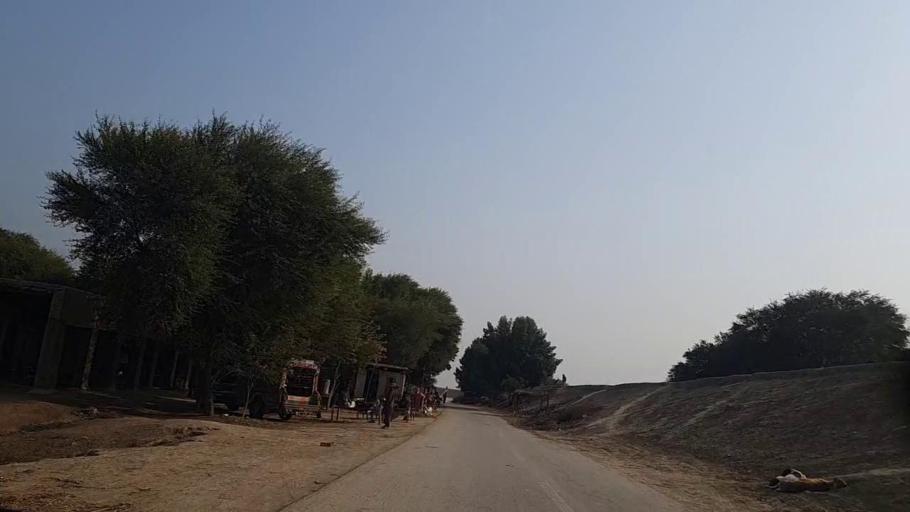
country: PK
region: Sindh
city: Sann
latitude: 26.1563
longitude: 68.1176
